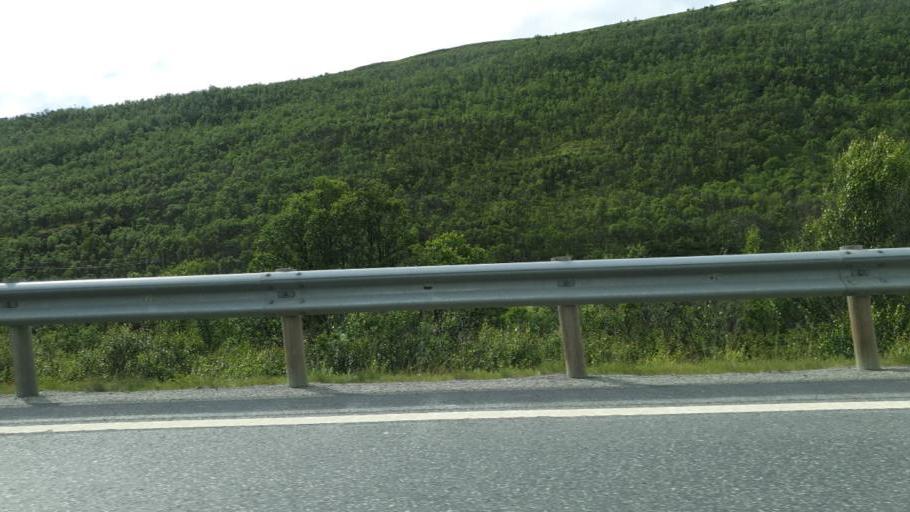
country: NO
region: Sor-Trondelag
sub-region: Oppdal
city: Oppdal
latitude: 62.3100
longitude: 9.6120
